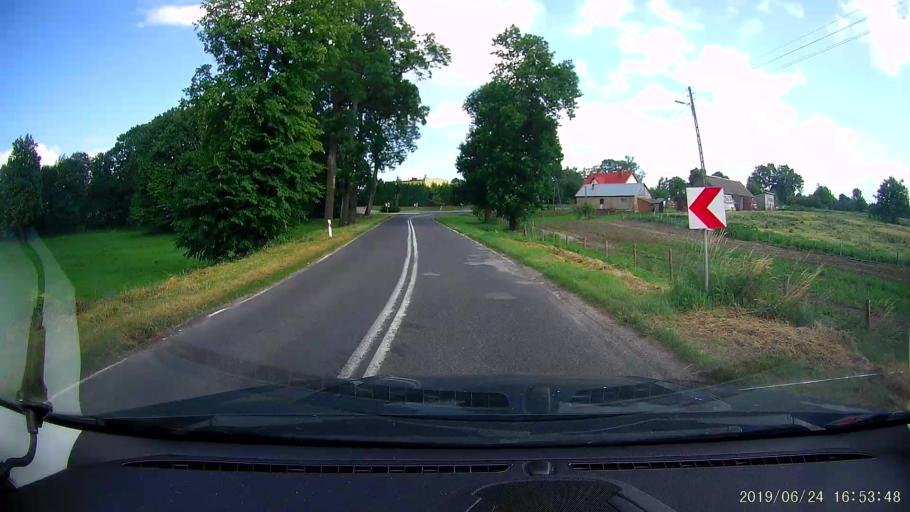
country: PL
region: Lublin Voivodeship
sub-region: Powiat tomaszowski
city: Telatyn
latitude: 50.5345
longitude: 23.8066
